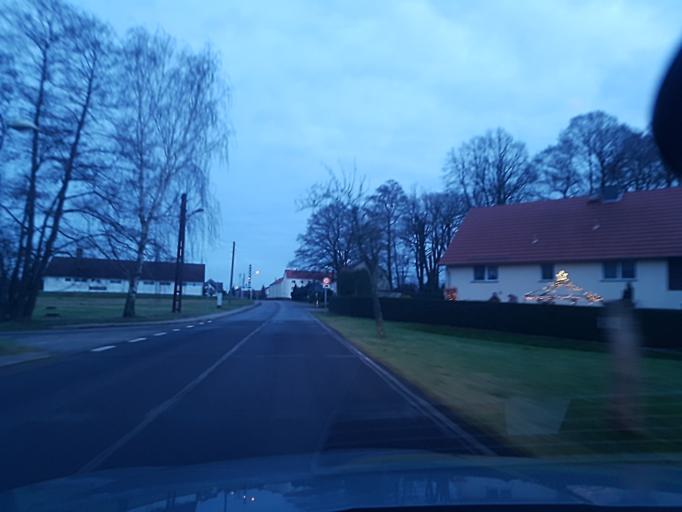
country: DE
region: Brandenburg
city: Ruckersdorf
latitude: 51.5718
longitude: 13.5661
